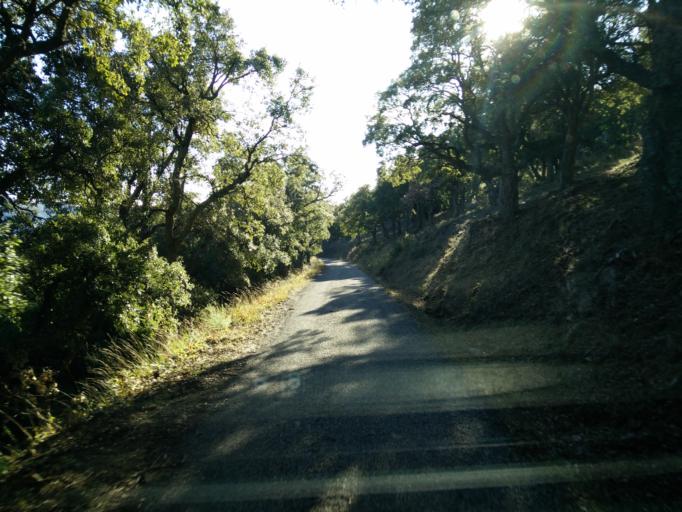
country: FR
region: Provence-Alpes-Cote d'Azur
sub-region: Departement du Var
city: Collobrieres
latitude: 43.2641
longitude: 6.2901
